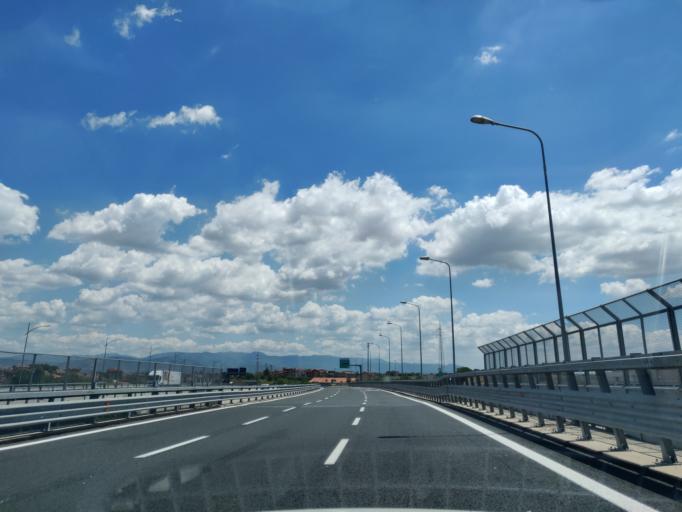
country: IT
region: Latium
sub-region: Citta metropolitana di Roma Capitale
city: Setteville
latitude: 41.9185
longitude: 12.6583
